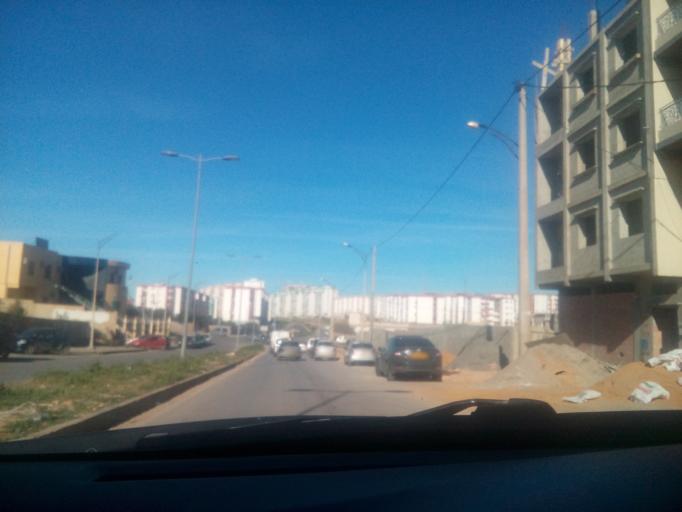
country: DZ
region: Oran
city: Bir el Djir
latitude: 35.7498
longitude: -0.5516
